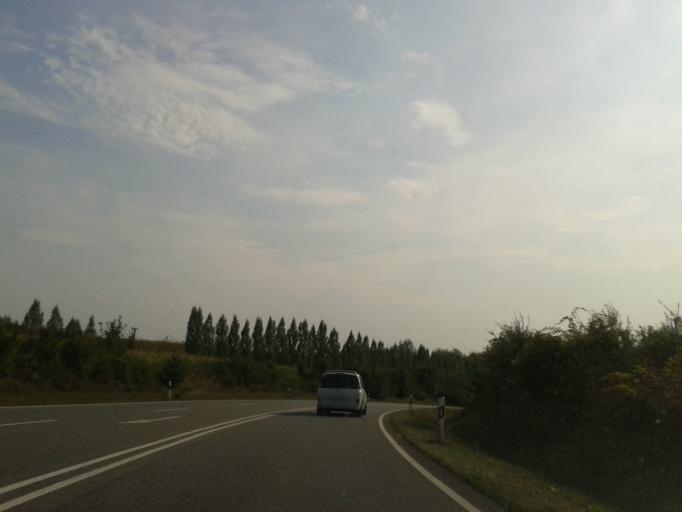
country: DE
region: Saxony
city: Freital
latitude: 51.0327
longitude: 13.6106
